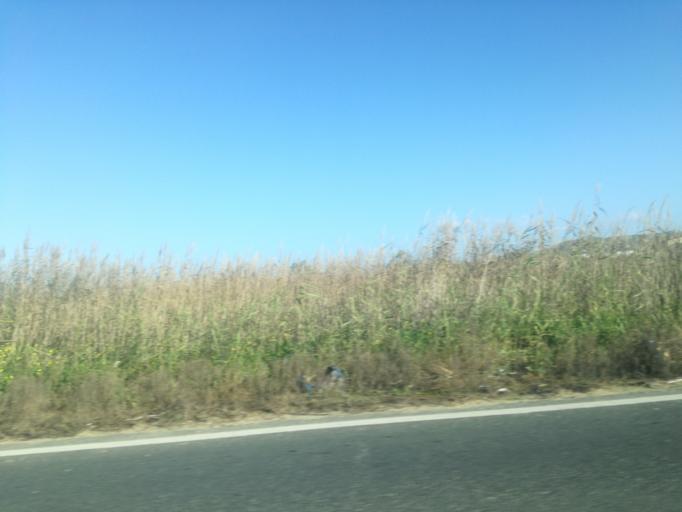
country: IT
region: Sicily
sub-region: Provincia di Caltanissetta
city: Gela
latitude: 37.0546
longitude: 14.3012
